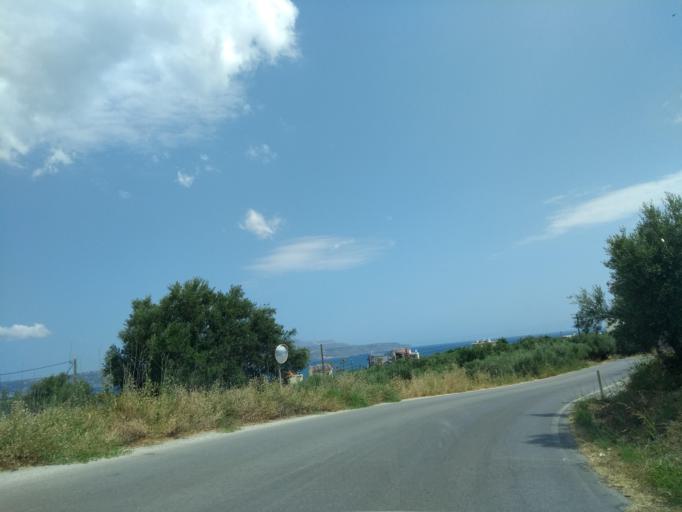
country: GR
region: Crete
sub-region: Nomos Chanias
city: Kalivai
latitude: 35.4456
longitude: 24.1748
